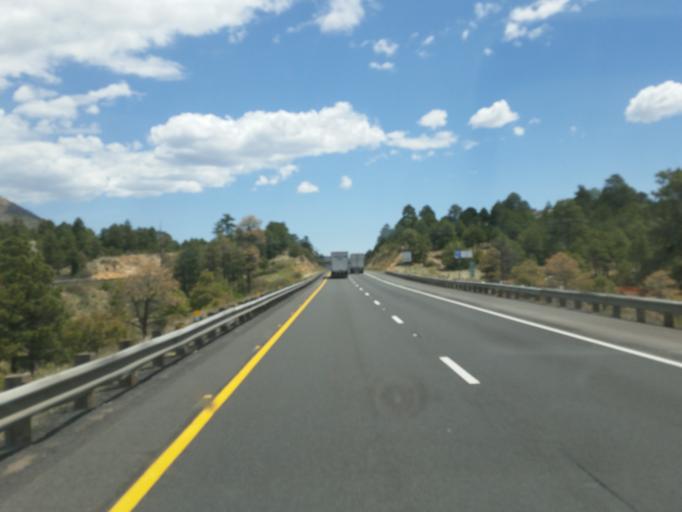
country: US
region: Arizona
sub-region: Coconino County
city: Flagstaff
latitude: 35.1983
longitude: -111.6125
